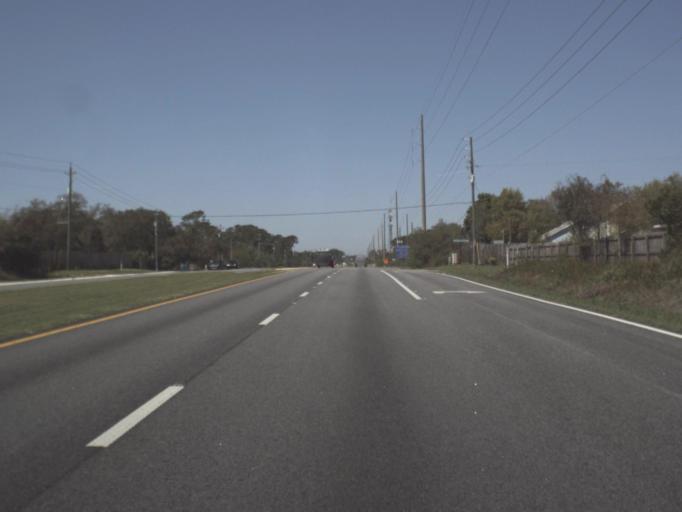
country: US
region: Florida
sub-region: Santa Rosa County
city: Navarre
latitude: 30.4106
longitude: -86.7789
